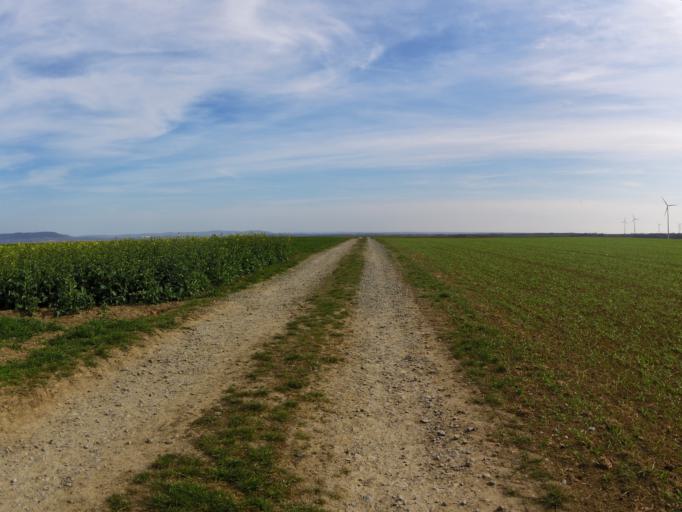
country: DE
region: Bavaria
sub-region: Regierungsbezirk Unterfranken
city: Mainstockheim
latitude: 49.7975
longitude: 10.1357
